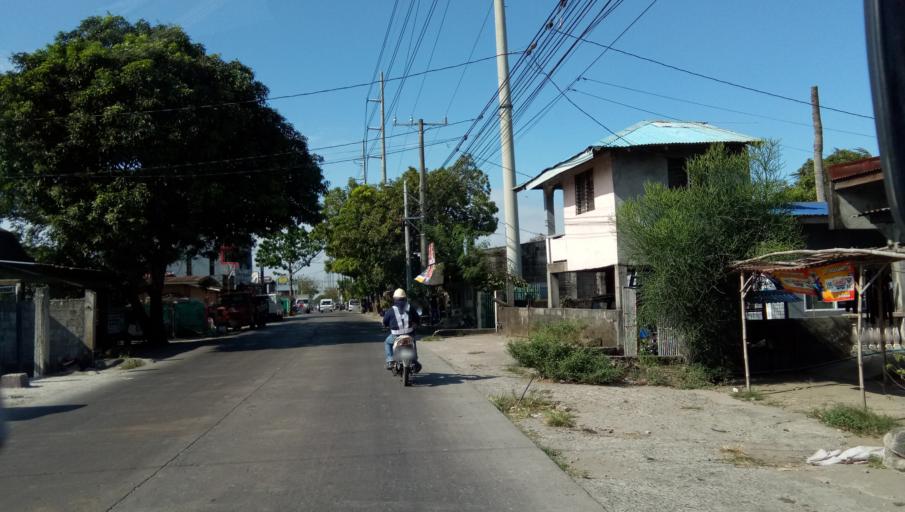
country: PH
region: Calabarzon
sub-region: Province of Cavite
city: Pasong Kawayan Primero
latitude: 14.3460
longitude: 120.9051
